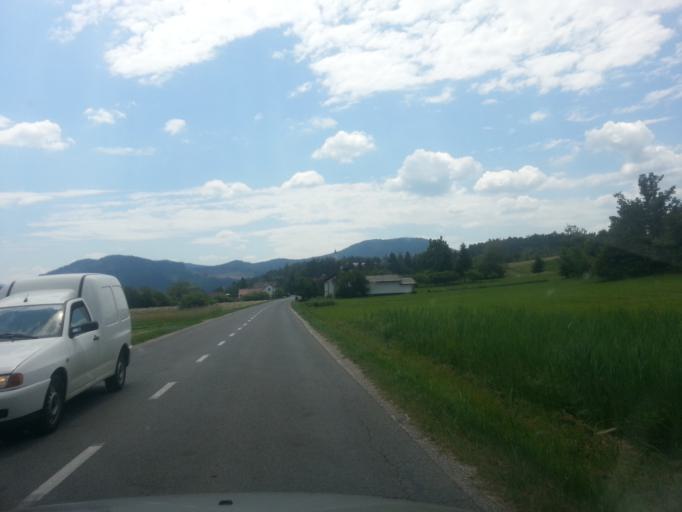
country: SI
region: Vrhnika
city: Vrhnika
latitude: 45.9782
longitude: 14.2899
